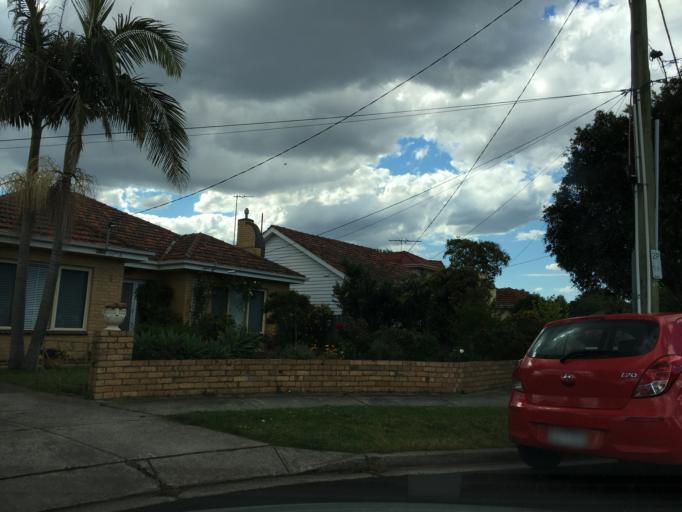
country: AU
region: Victoria
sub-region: Monash
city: Oakleigh South
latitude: -37.9130
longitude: 145.0996
